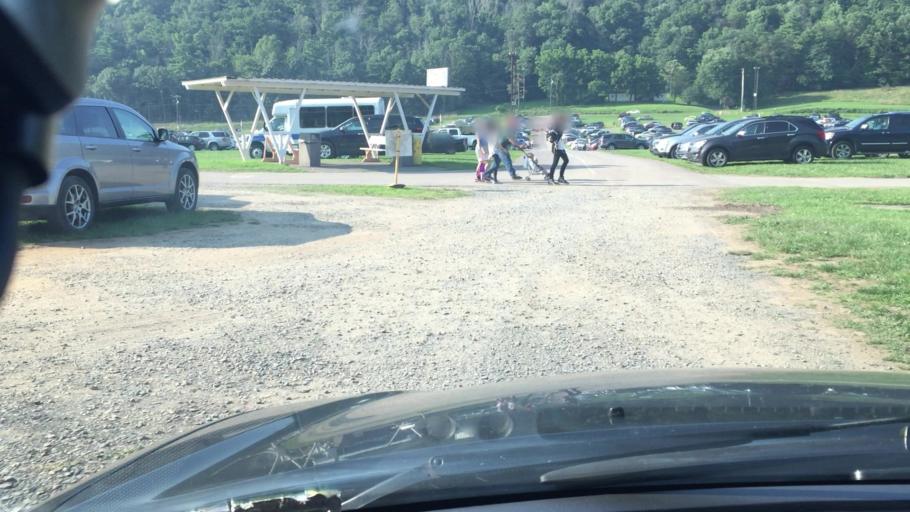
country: US
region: Pennsylvania
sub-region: Northumberland County
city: Elysburg
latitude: 40.8772
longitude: -76.4978
